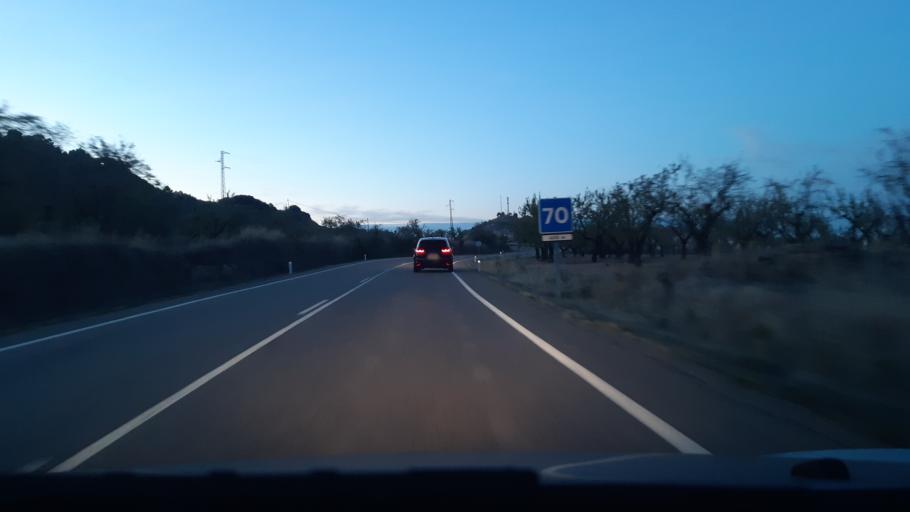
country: ES
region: Aragon
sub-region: Provincia de Teruel
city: Calaceite
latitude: 41.0076
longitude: 0.1912
